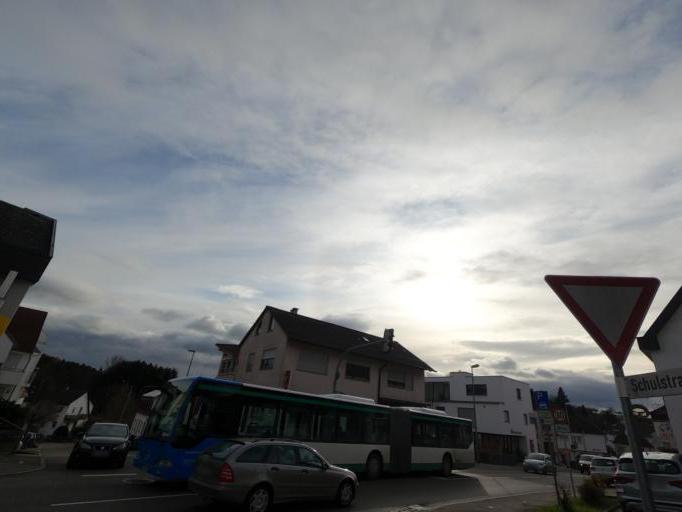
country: DE
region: Baden-Wuerttemberg
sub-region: Regierungsbezirk Stuttgart
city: Albershausen
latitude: 48.6930
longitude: 9.5666
